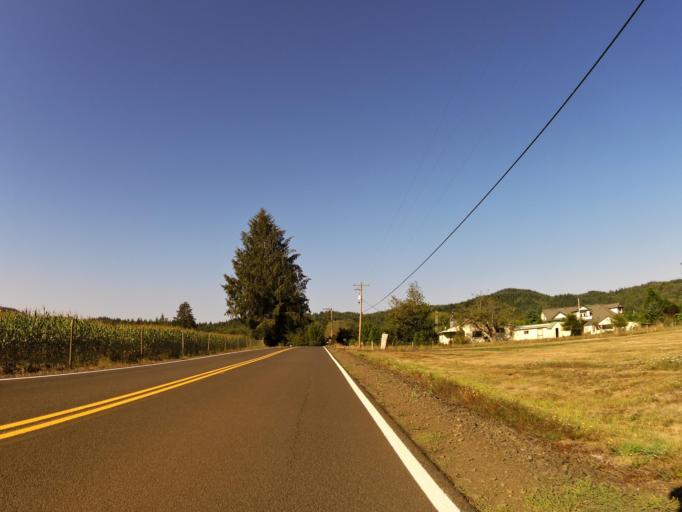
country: US
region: Oregon
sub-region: Tillamook County
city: Tillamook
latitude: 45.3854
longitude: -123.7976
